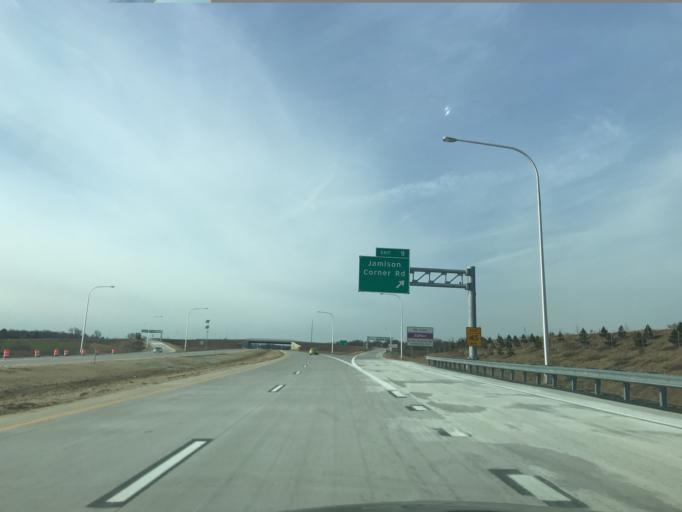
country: US
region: Delaware
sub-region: New Castle County
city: Middletown
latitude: 39.5254
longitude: -75.6731
